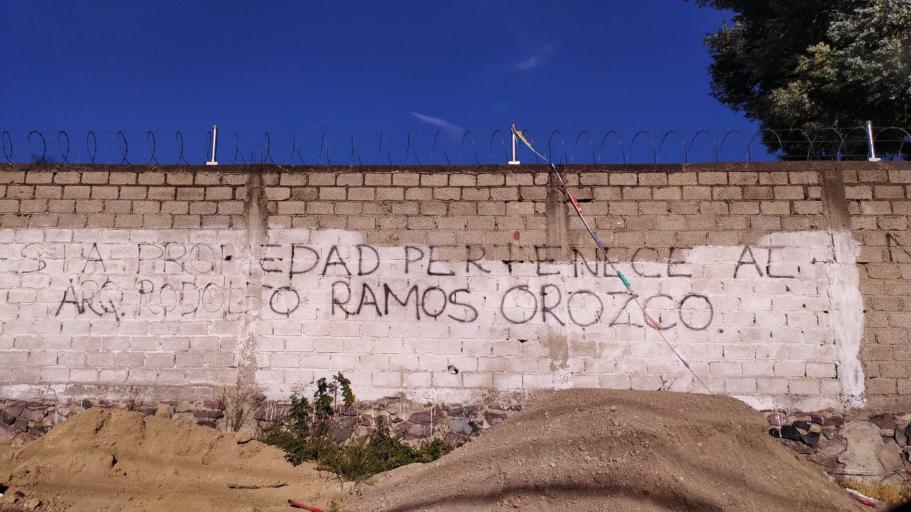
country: MX
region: Jalisco
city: Guadalajara
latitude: 20.6632
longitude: -103.4356
